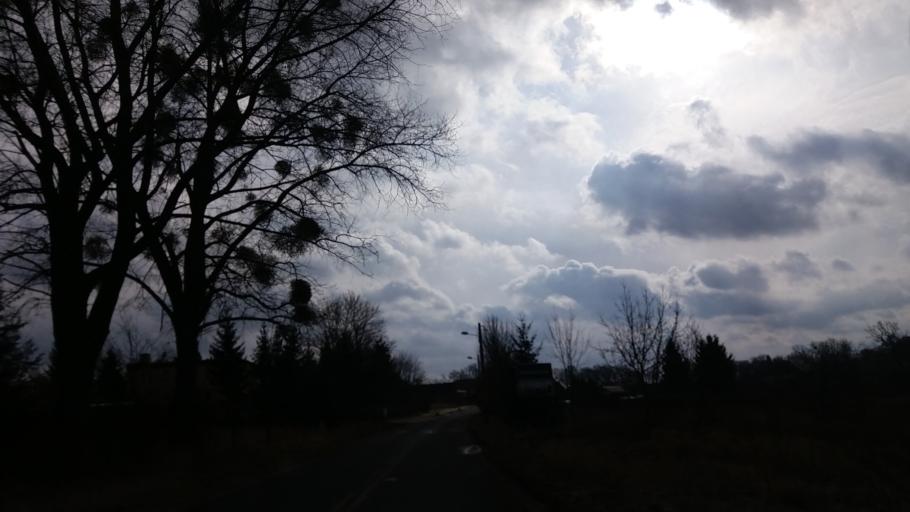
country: PL
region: West Pomeranian Voivodeship
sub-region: Powiat choszczenski
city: Drawno
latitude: 53.2569
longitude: 15.7090
